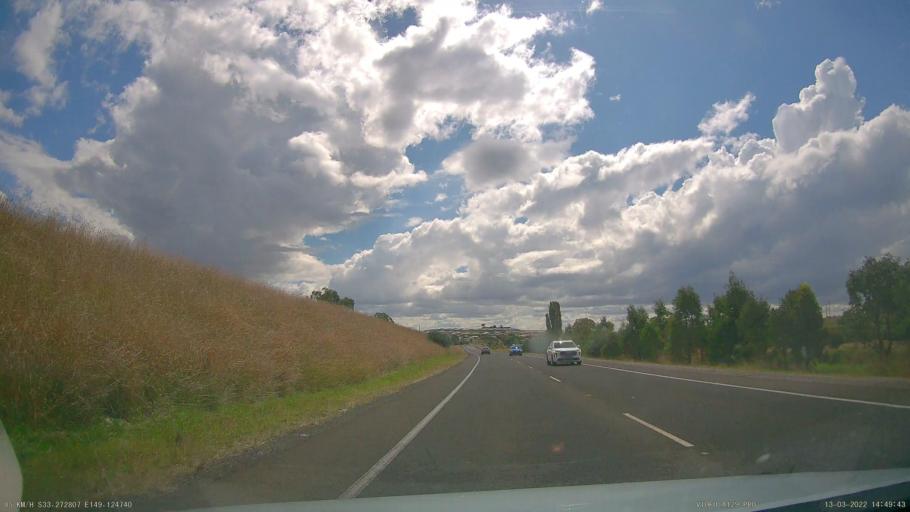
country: AU
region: New South Wales
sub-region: Orange Municipality
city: Orange
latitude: -33.2726
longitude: 149.1244
